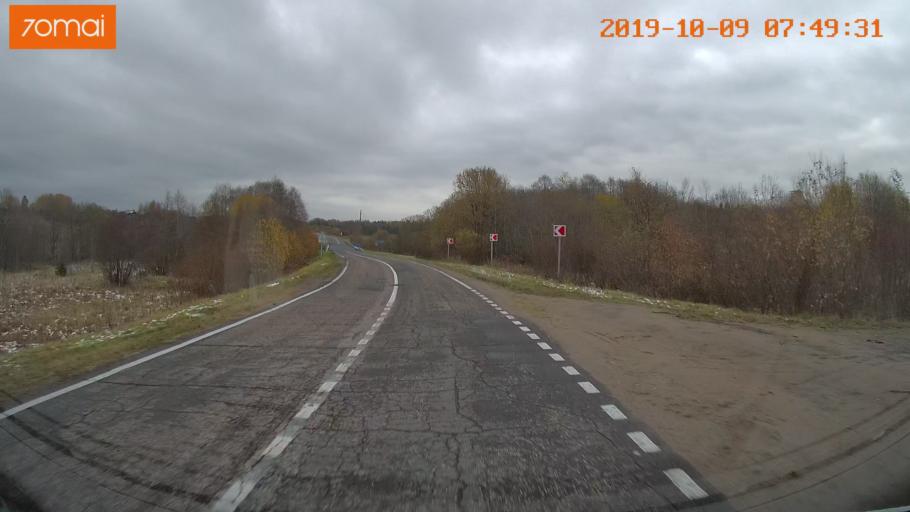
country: RU
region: Jaroslavl
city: Kukoboy
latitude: 58.6673
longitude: 39.8488
